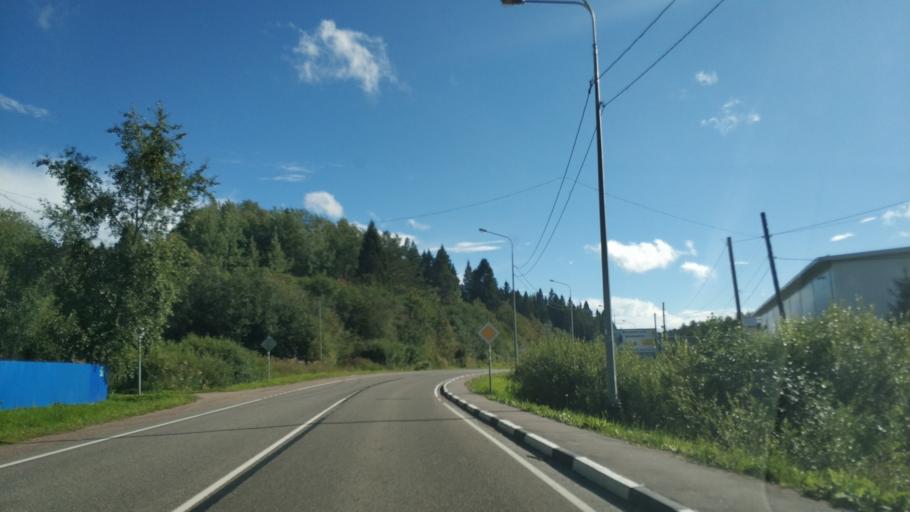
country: RU
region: Republic of Karelia
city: Sortavala
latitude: 61.6763
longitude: 30.6551
